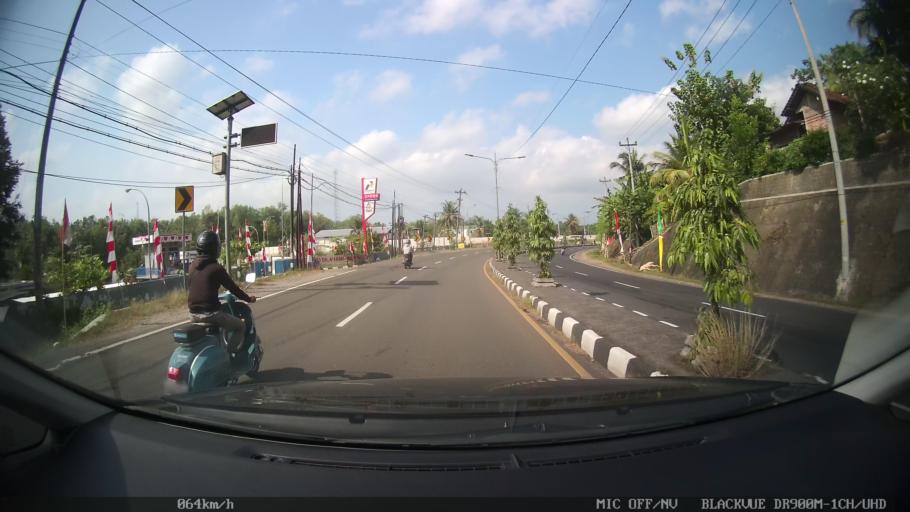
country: ID
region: Daerah Istimewa Yogyakarta
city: Srandakan
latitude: -7.8543
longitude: 110.2159
